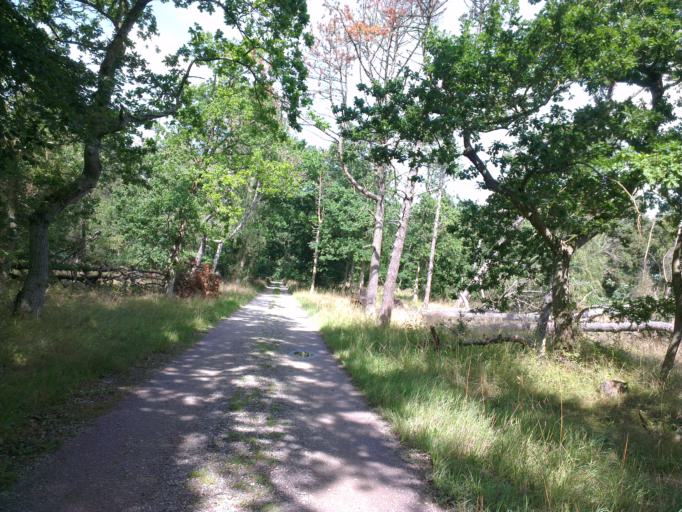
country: DK
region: Capital Region
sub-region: Frederikssund Kommune
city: Jaegerspris
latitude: 55.8479
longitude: 11.9645
